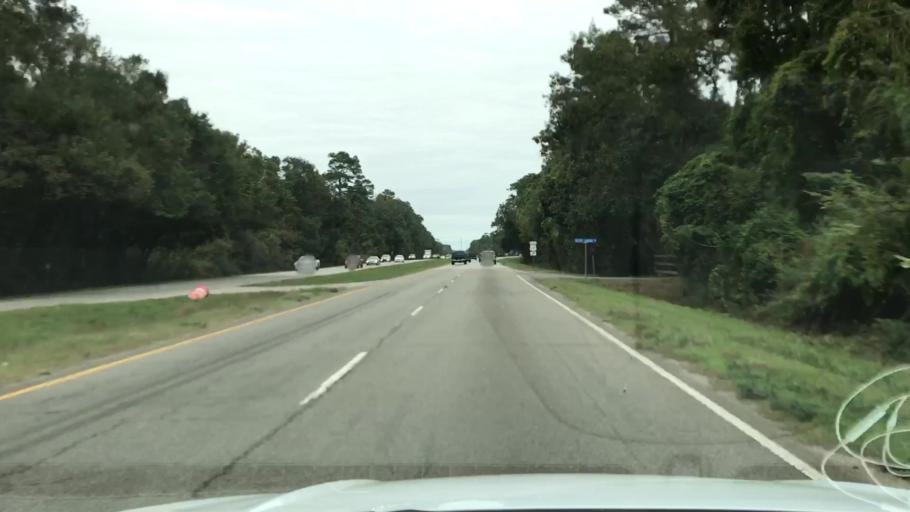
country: US
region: South Carolina
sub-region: Georgetown County
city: Murrells Inlet
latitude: 33.5243
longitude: -79.0656
